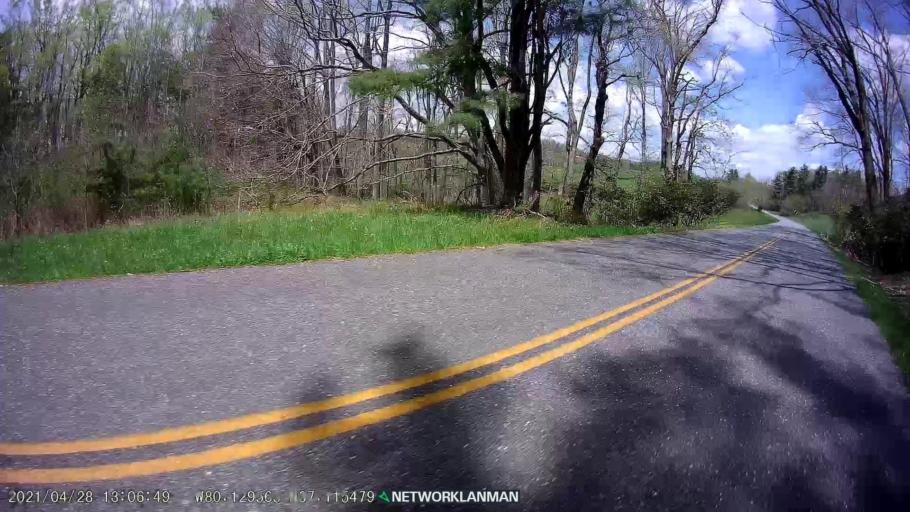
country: US
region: Virginia
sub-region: Montgomery County
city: Shawsville
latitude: 37.1161
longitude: -80.1296
